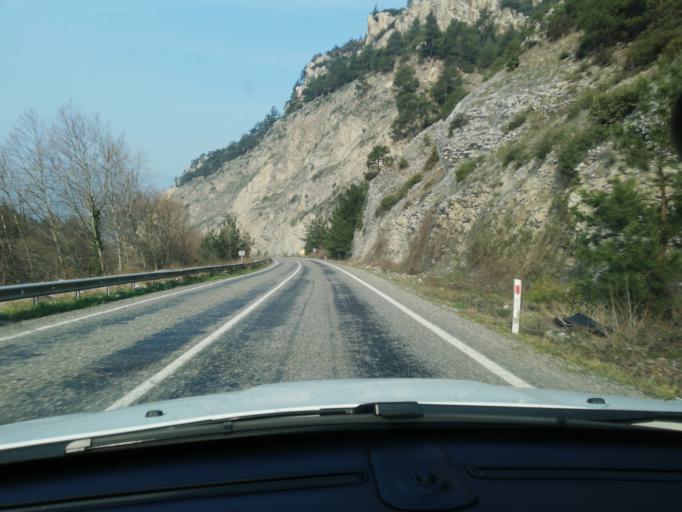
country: TR
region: Karabuk
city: Karabuk
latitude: 41.1601
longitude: 32.5565
